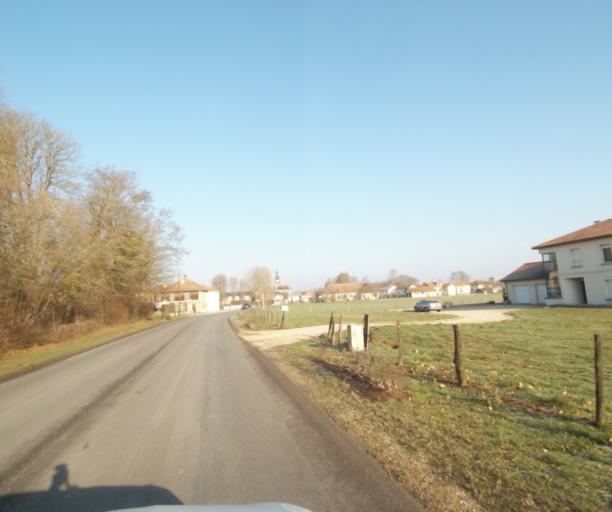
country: FR
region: Champagne-Ardenne
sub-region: Departement de la Haute-Marne
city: Montier-en-Der
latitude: 48.4680
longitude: 4.7635
